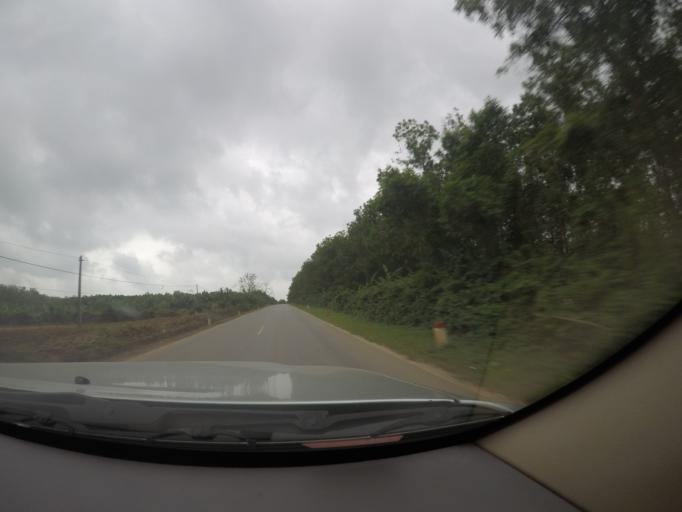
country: VN
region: Quang Tri
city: Cam Lo
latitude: 16.9003
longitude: 106.9841
